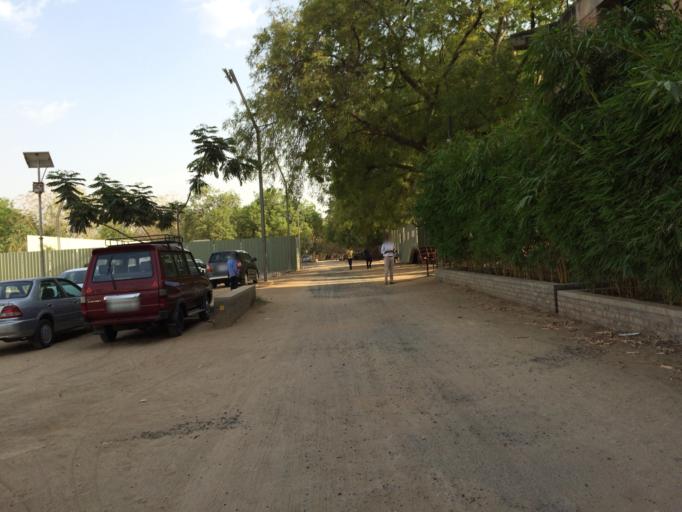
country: IN
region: Gujarat
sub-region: Ahmadabad
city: Ahmedabad
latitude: 23.0377
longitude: 72.5504
